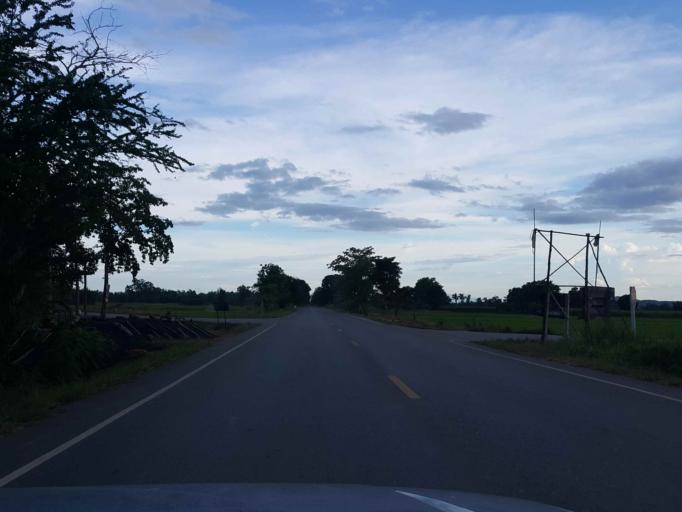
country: TH
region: Sukhothai
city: Sawankhalok
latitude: 17.3664
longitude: 99.7417
